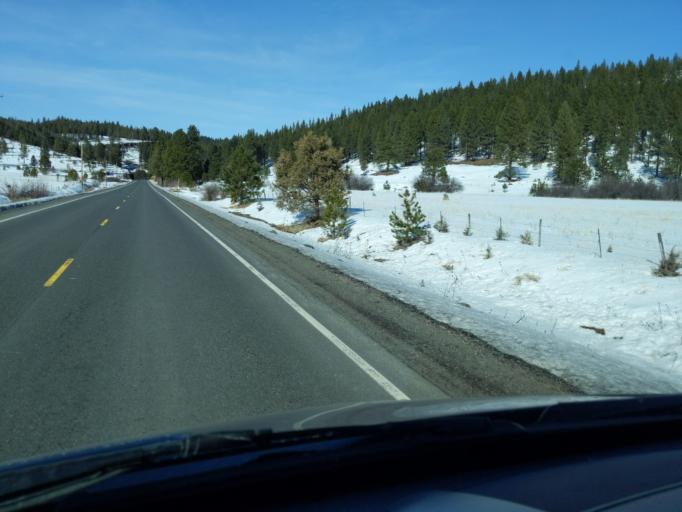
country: US
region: Oregon
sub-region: Grant County
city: John Day
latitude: 44.9285
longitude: -119.0103
